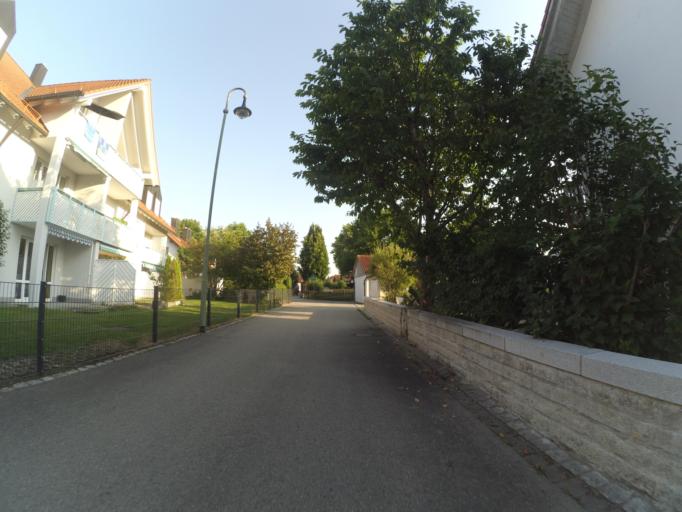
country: DE
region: Bavaria
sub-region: Swabia
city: Buchloe
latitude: 48.0388
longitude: 10.7099
